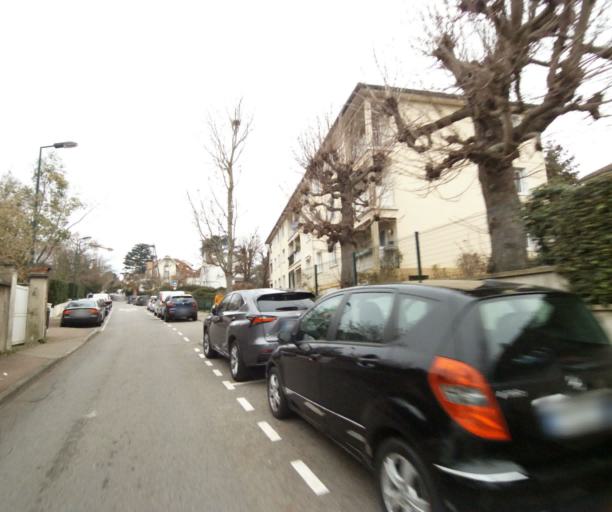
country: FR
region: Ile-de-France
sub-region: Departement des Hauts-de-Seine
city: Garches
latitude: 48.8463
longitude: 2.1843
